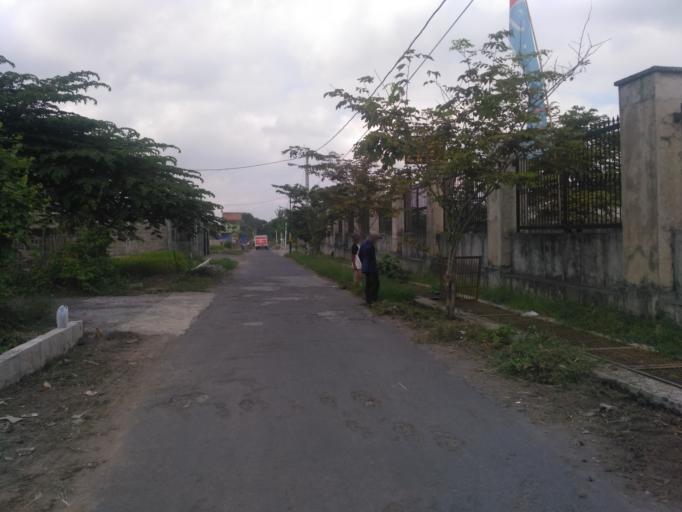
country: ID
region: Daerah Istimewa Yogyakarta
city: Melati
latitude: -7.7490
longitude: 110.3559
